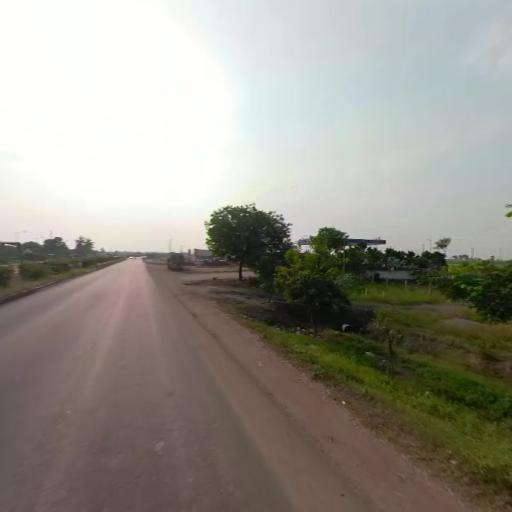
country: IN
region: Telangana
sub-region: Nalgonda
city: Suriapet
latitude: 17.1608
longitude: 79.5207
